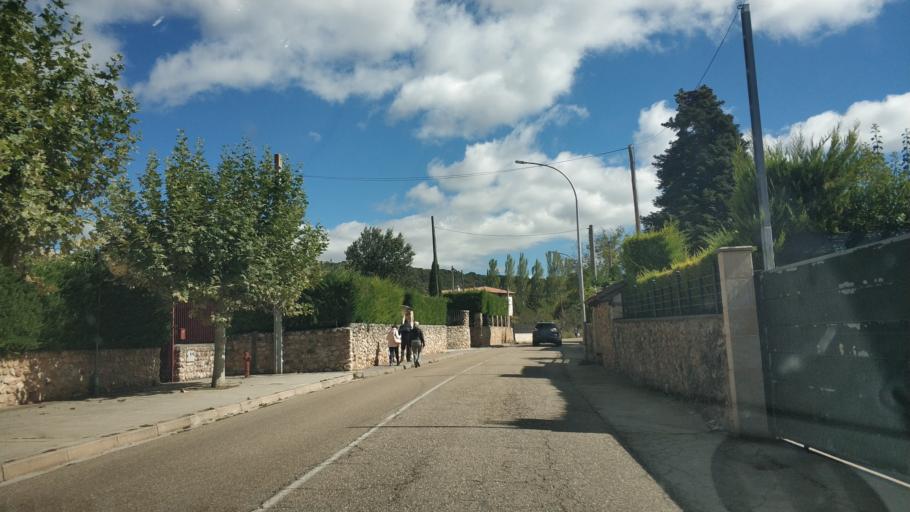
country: ES
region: Castille and Leon
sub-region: Provincia de Burgos
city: Covarrubias
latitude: 42.0600
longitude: -3.5161
